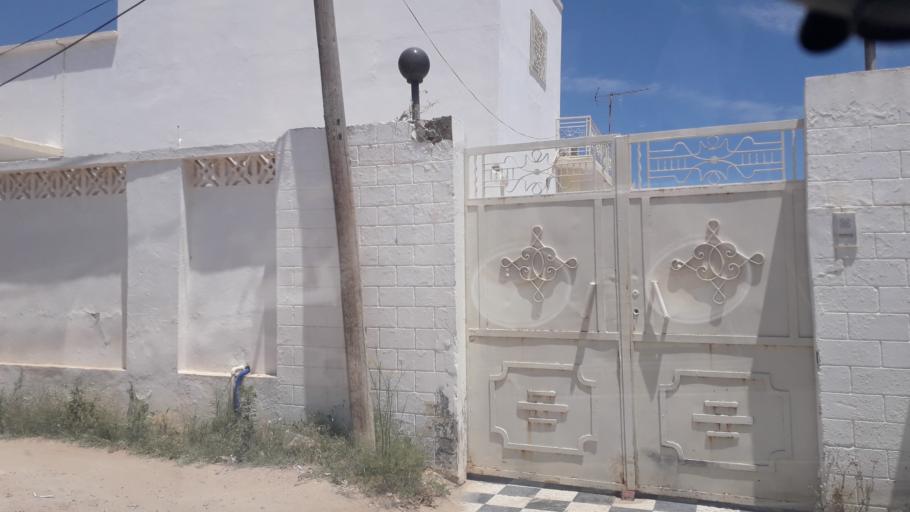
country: TN
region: Safaqis
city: Al Qarmadah
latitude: 34.8173
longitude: 10.7635
